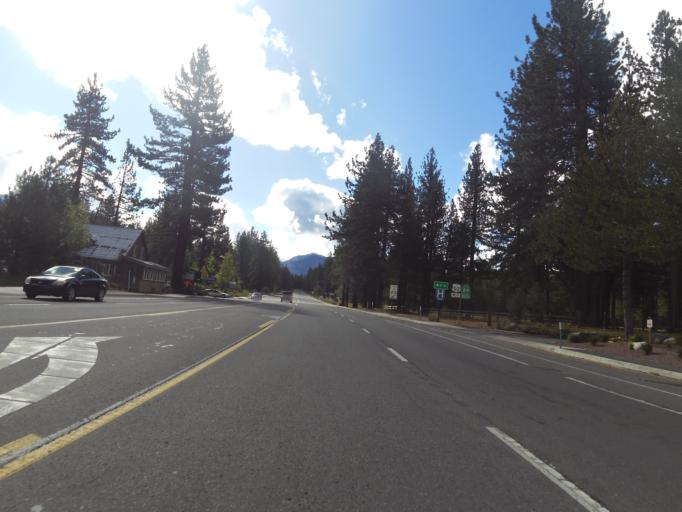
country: US
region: California
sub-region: El Dorado County
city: South Lake Tahoe
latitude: 38.9114
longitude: -120.0036
